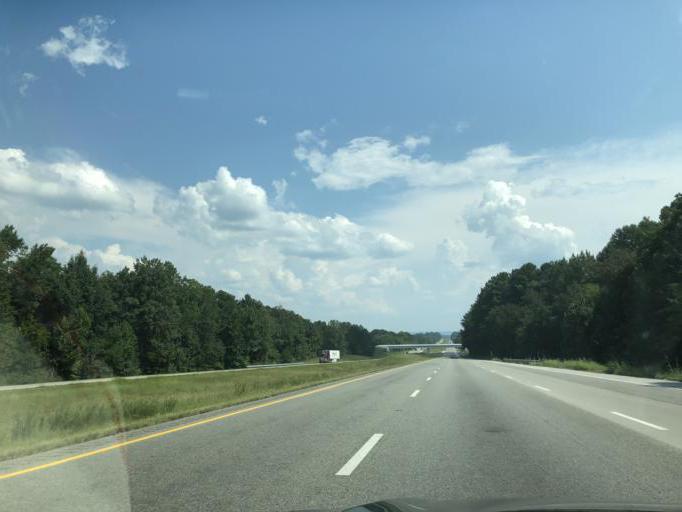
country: US
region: Tennessee
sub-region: Coffee County
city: Manchester
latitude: 35.3871
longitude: -85.9860
